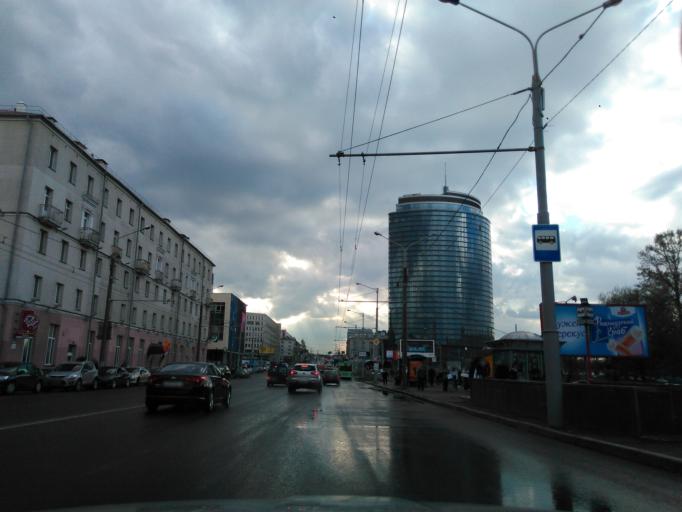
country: BY
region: Minsk
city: Minsk
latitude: 53.9055
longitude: 27.5379
